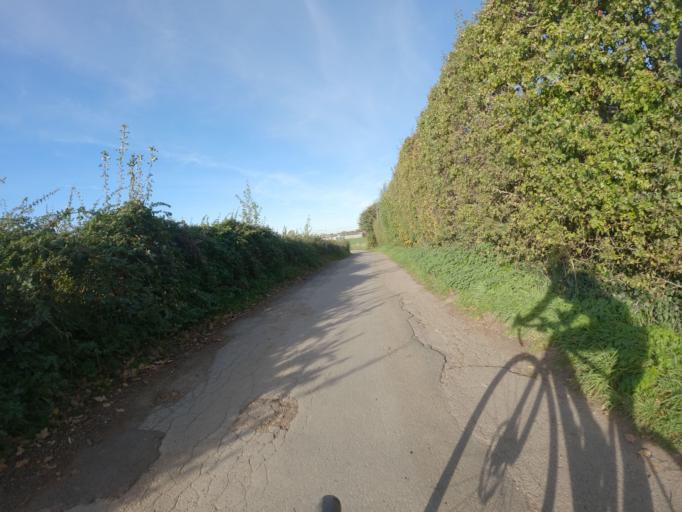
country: DE
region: North Rhine-Westphalia
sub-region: Regierungsbezirk Koln
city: Aachen
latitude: 50.8192
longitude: 6.0869
